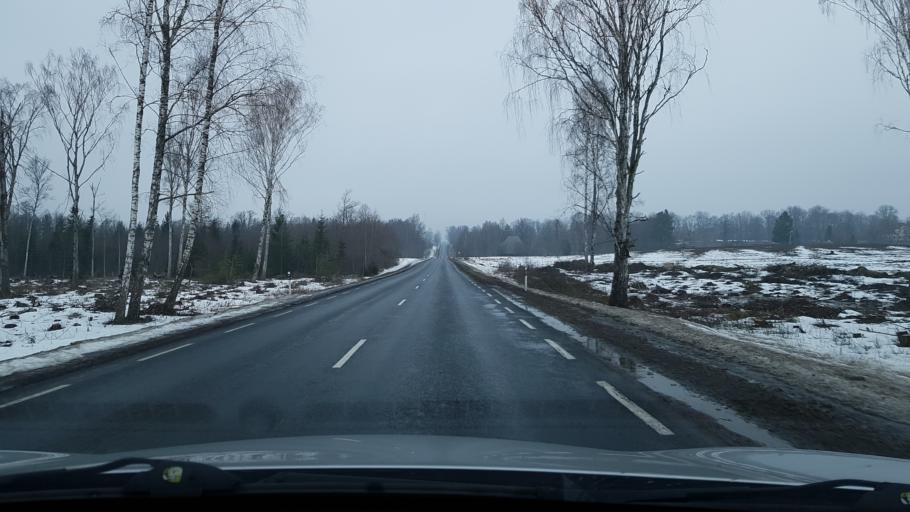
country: EE
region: Valgamaa
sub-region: Torva linn
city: Torva
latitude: 58.1437
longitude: 25.9837
